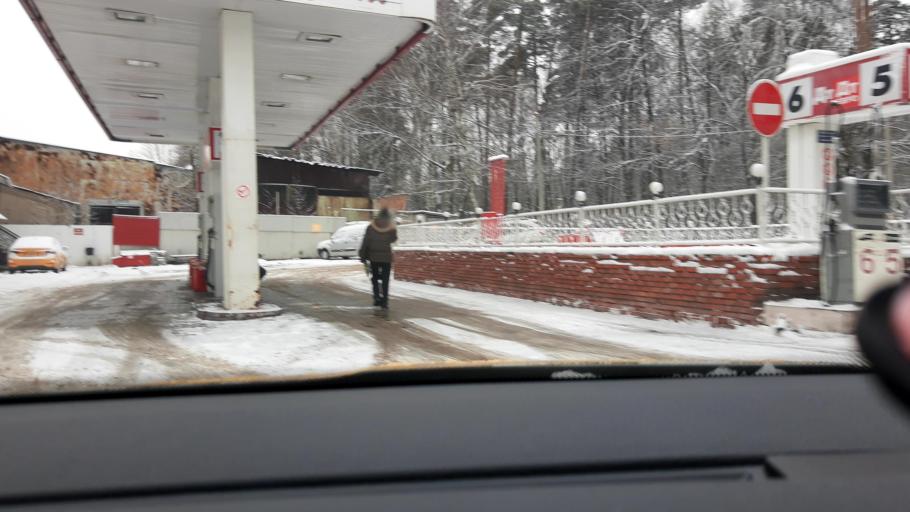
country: RU
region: Moskovskaya
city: Ivanteyevka
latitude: 55.9736
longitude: 37.8956
